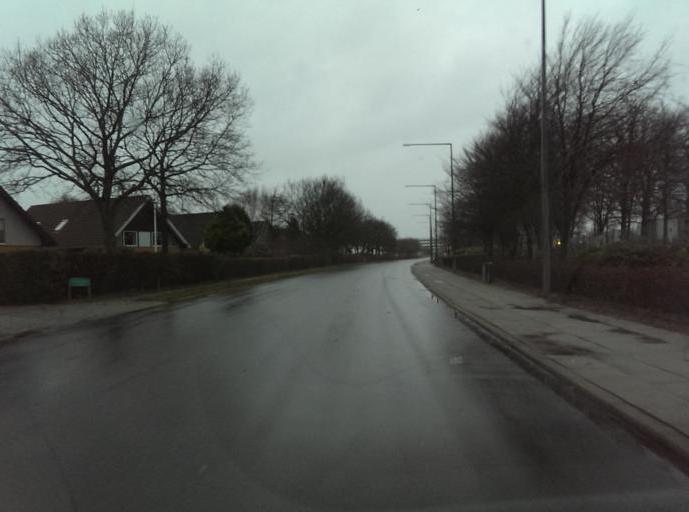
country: DK
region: South Denmark
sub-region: Esbjerg Kommune
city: Esbjerg
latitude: 55.4834
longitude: 8.4953
